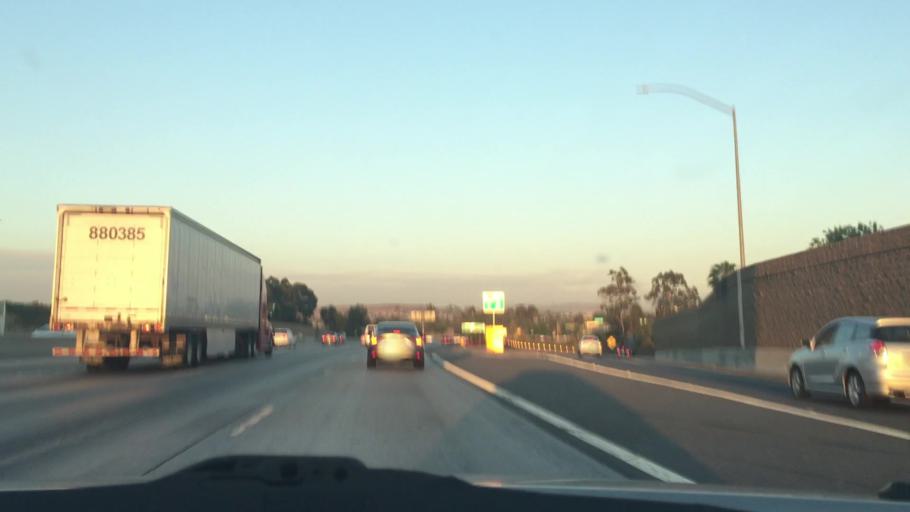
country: US
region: California
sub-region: Los Angeles County
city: Belvedere
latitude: 34.0362
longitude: -118.1544
